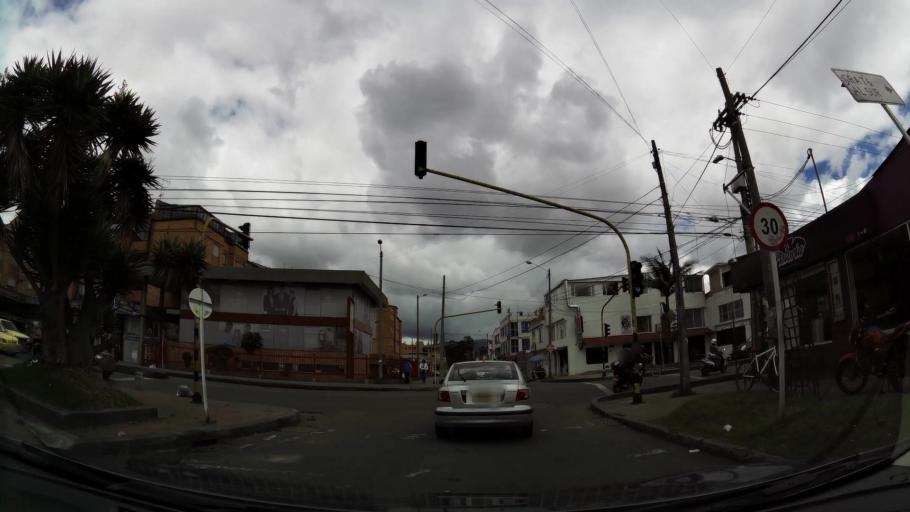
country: CO
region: Bogota D.C.
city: Barrio San Luis
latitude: 4.7010
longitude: -74.0920
